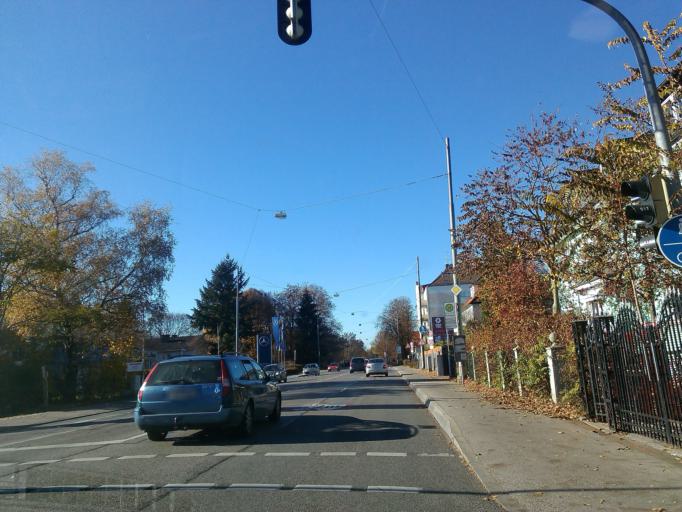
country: DE
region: Bavaria
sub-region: Upper Bavaria
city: Pasing
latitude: 48.1461
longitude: 11.4465
